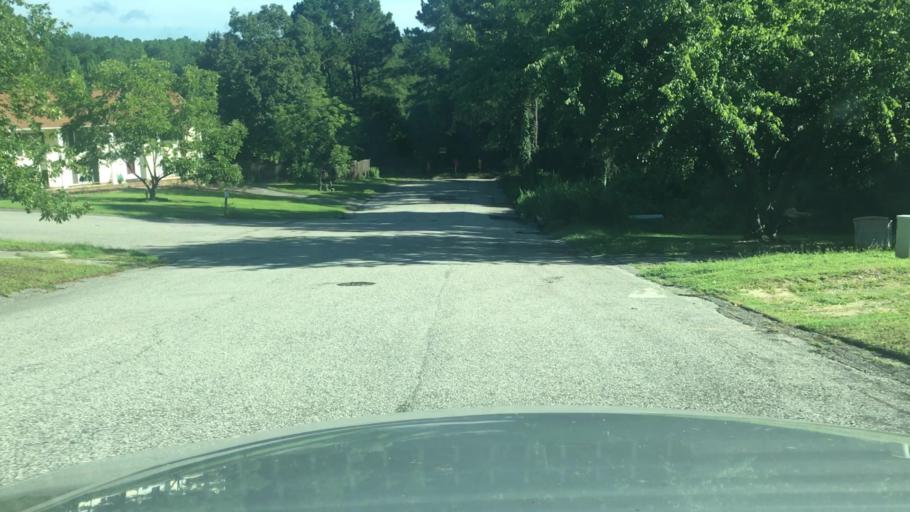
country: US
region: North Carolina
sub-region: Cumberland County
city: Spring Lake
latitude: 35.1391
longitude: -78.8919
